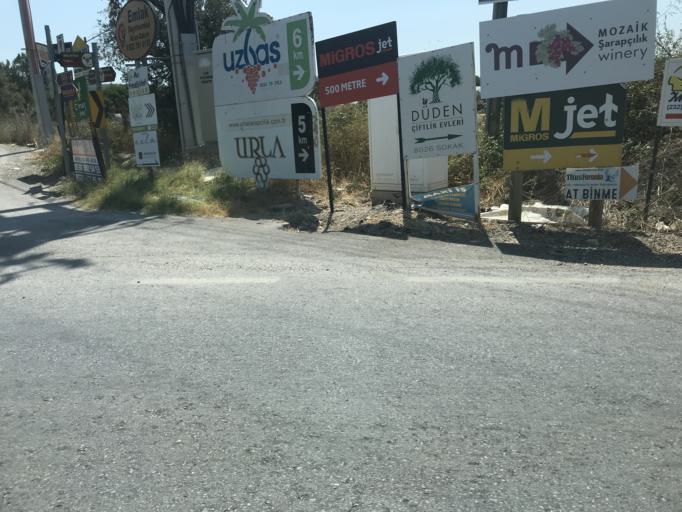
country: TR
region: Izmir
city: Urla
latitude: 38.2866
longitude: 26.7528
